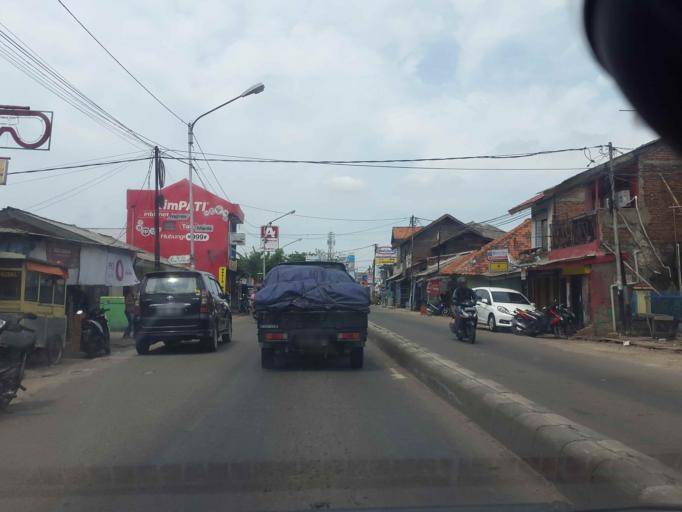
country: ID
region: Banten
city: Tangerang
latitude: -6.1631
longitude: 106.6440
